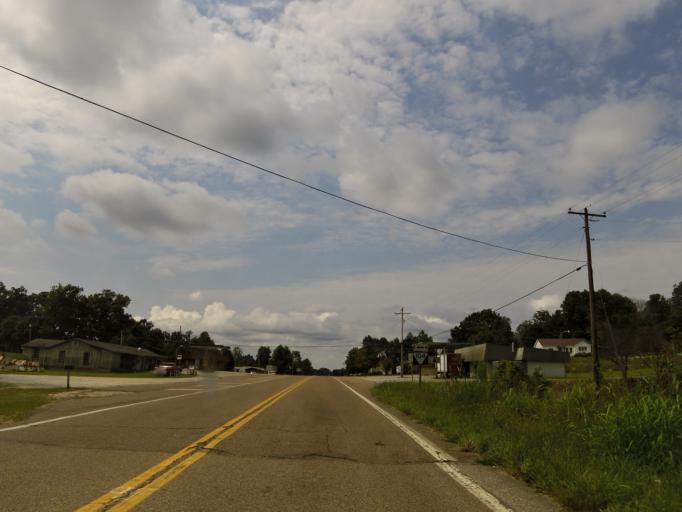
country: US
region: Tennessee
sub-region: Henderson County
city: Lexington
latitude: 35.5089
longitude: -88.3226
